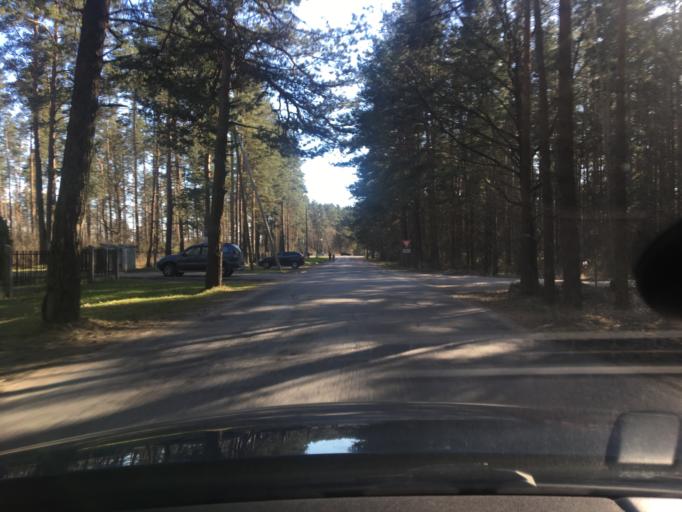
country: LV
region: Salaspils
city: Salaspils
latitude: 56.8626
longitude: 24.3058
